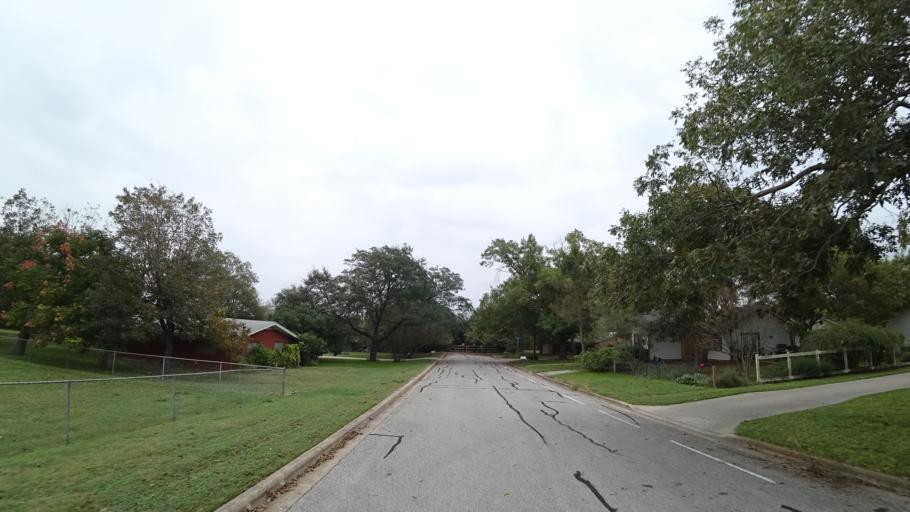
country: US
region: Texas
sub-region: Travis County
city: Pflugerville
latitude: 30.4367
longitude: -97.6163
